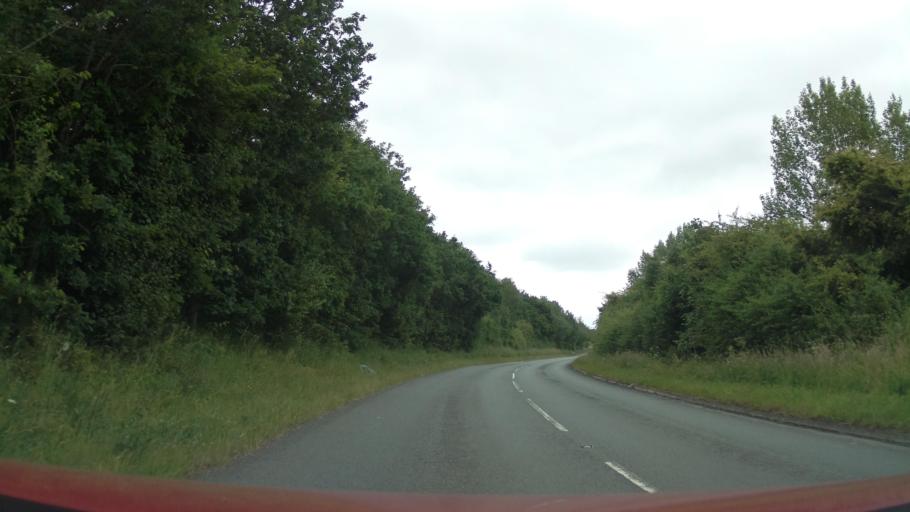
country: GB
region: England
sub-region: Derbyshire
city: Rodsley
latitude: 52.8812
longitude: -1.7099
